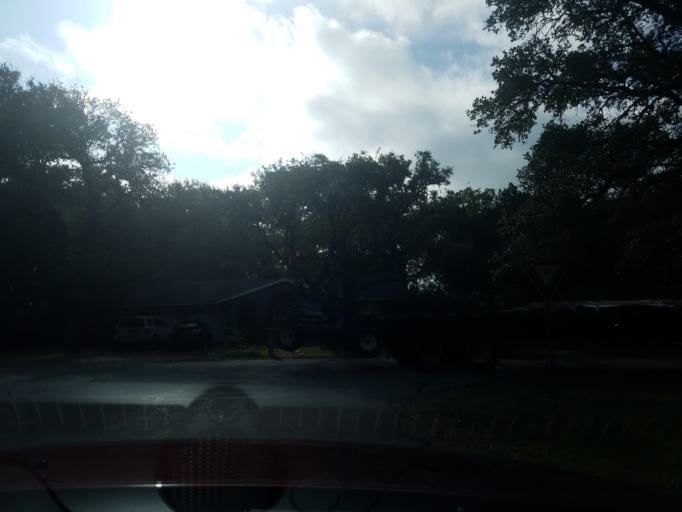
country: US
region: Texas
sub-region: Williamson County
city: Jollyville
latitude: 30.4528
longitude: -97.7826
